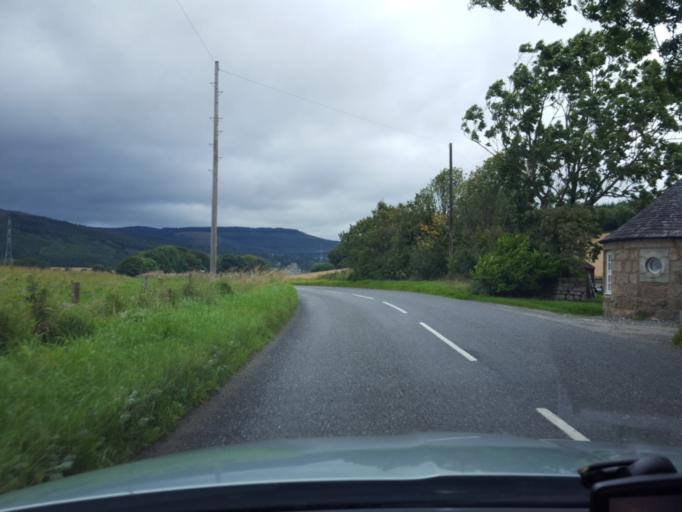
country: GB
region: Scotland
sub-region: Aberdeenshire
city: Kemnay
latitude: 57.1411
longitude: -2.4415
